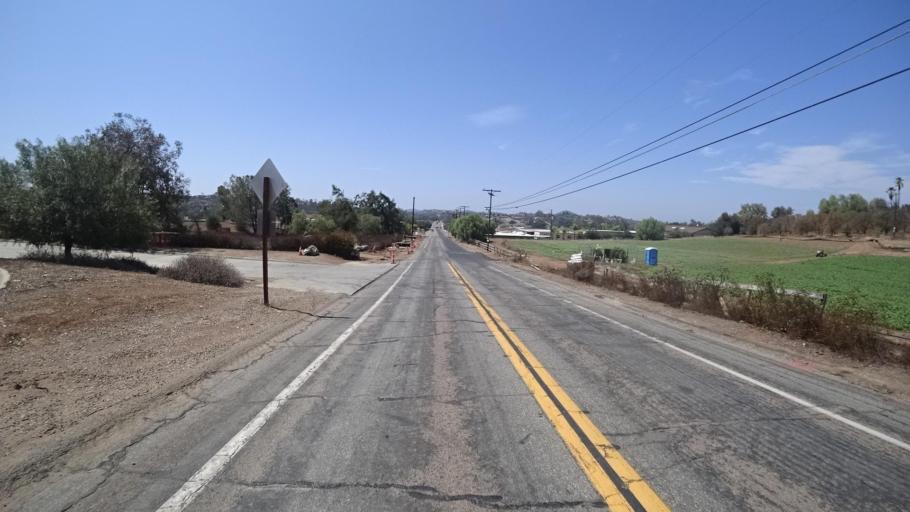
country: US
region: California
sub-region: San Diego County
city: Valley Center
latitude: 33.2315
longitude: -117.0187
